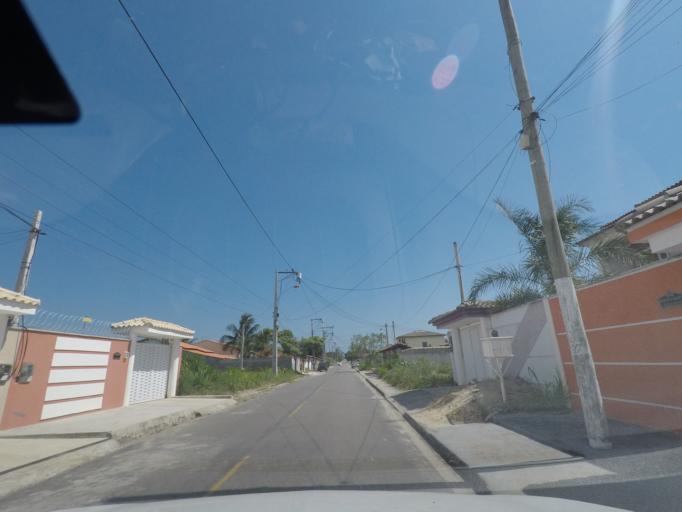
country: BR
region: Rio de Janeiro
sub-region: Marica
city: Marica
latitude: -22.9603
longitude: -42.9649
